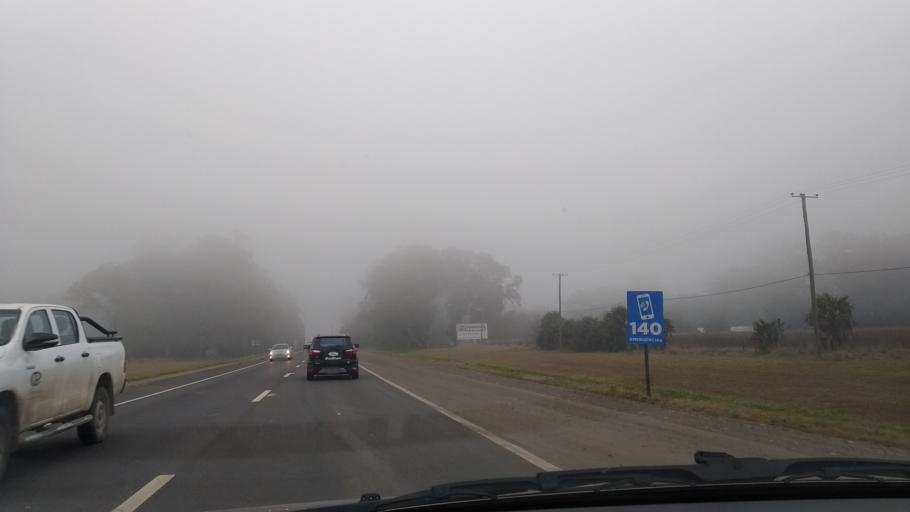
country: AR
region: Buenos Aires
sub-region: Partido de Azul
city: Azul
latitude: -36.8200
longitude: -59.8736
